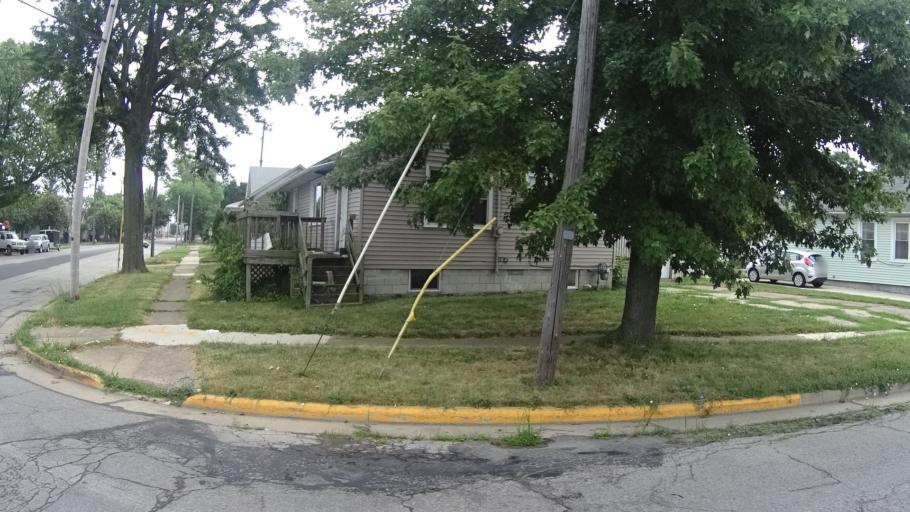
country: US
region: Ohio
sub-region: Erie County
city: Sandusky
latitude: 41.4526
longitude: -82.7222
